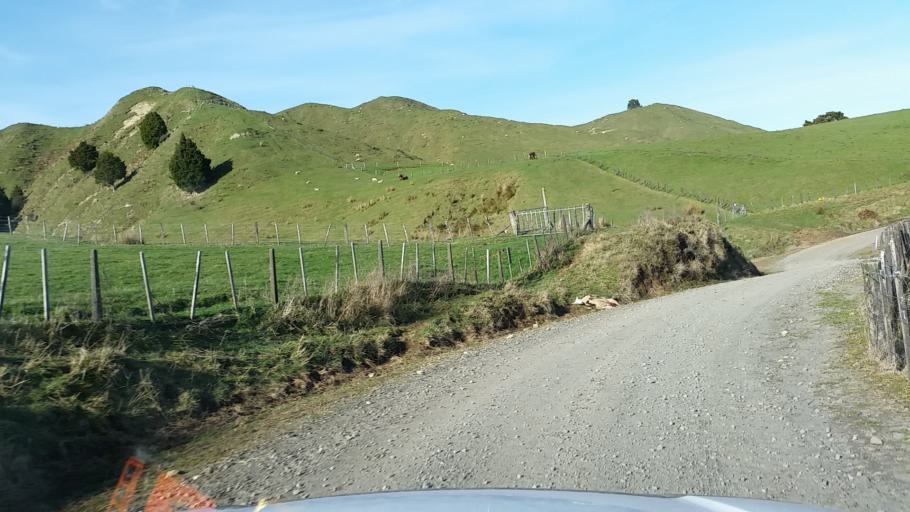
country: NZ
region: Taranaki
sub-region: South Taranaki District
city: Eltham
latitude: -39.3132
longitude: 174.5357
